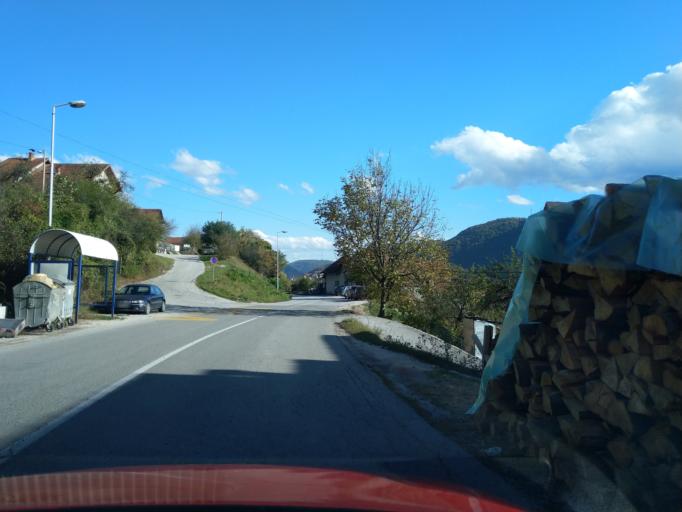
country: RS
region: Central Serbia
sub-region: Zlatiborski Okrug
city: Uzice
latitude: 43.8633
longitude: 19.8145
